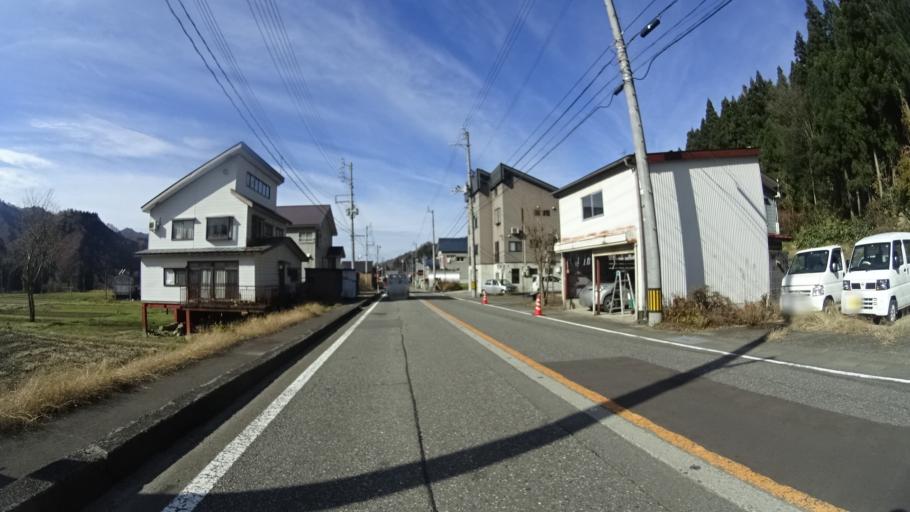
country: JP
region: Niigata
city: Muikamachi
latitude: 37.2090
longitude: 139.0601
